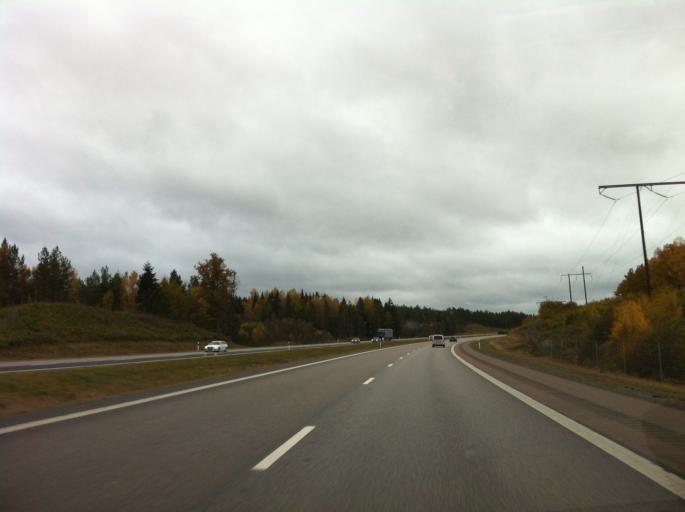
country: SE
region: OEstergoetland
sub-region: Vadstena Kommun
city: Herrestad
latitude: 58.2704
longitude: 14.8614
